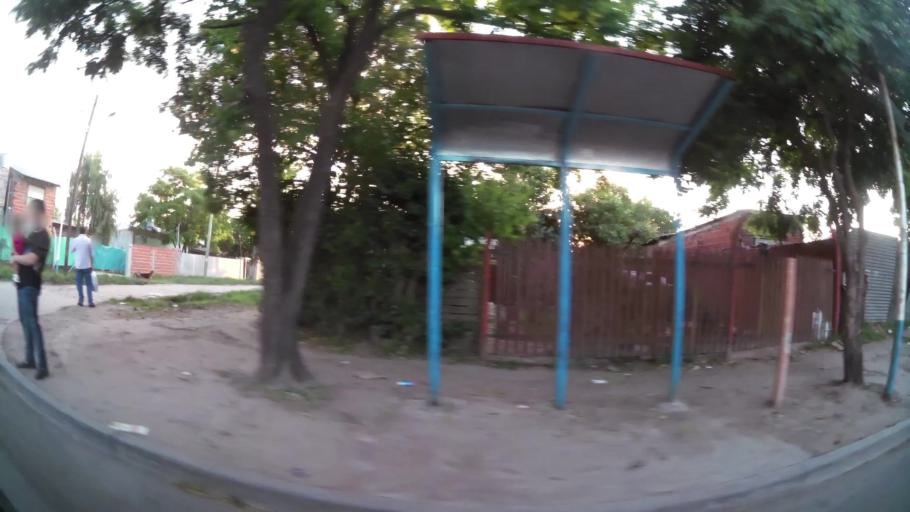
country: AR
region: Buenos Aires
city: Santa Catalina - Dique Lujan
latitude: -34.4816
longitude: -58.7527
